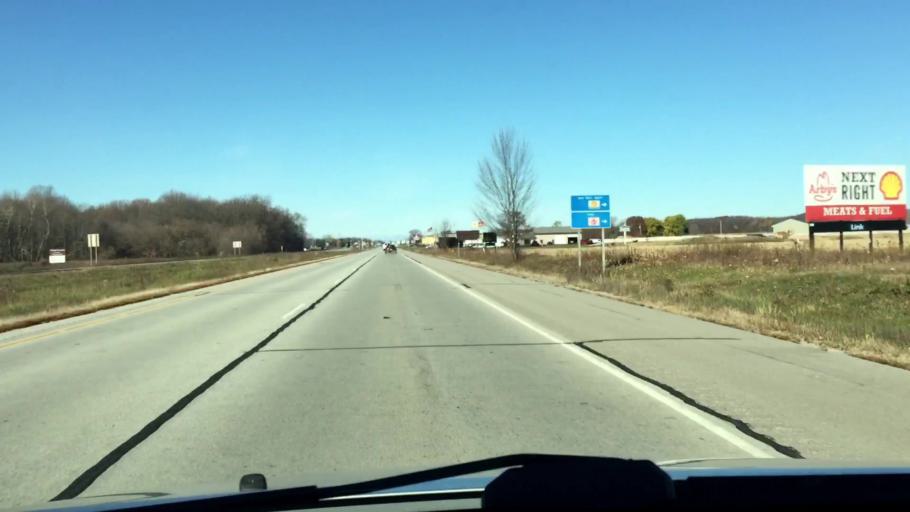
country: US
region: Wisconsin
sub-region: Brown County
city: Howard
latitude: 44.5707
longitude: -88.1559
